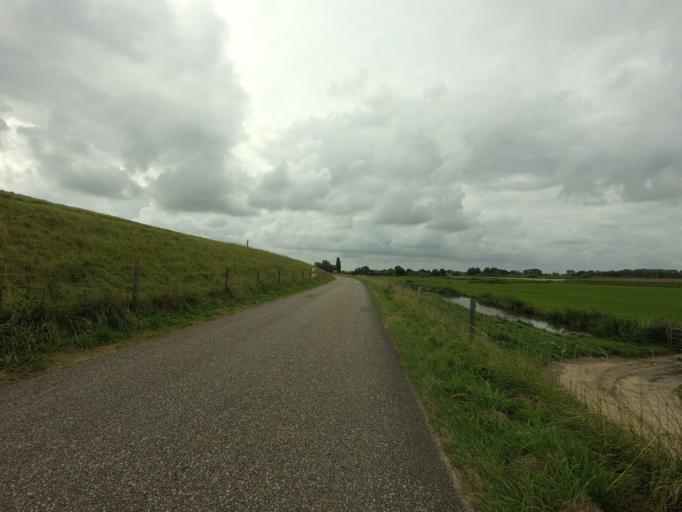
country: NL
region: North Holland
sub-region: Gemeente Hoorn
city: Hoorn
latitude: 52.6059
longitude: 5.0149
